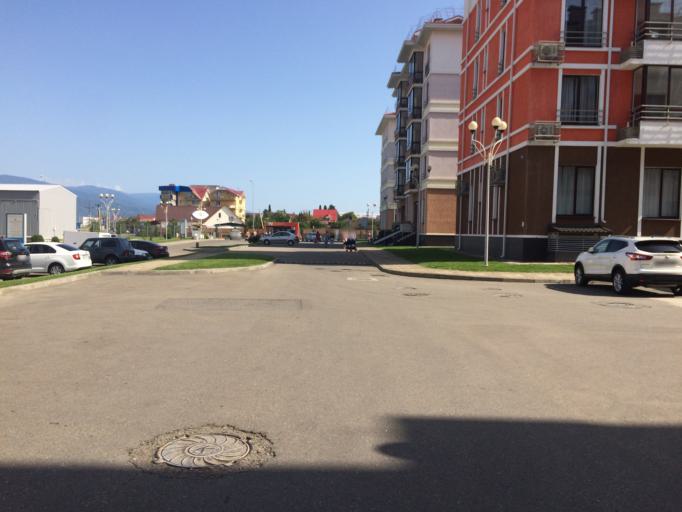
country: RU
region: Krasnodarskiy
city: Adler
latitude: 43.3961
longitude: 39.9782
